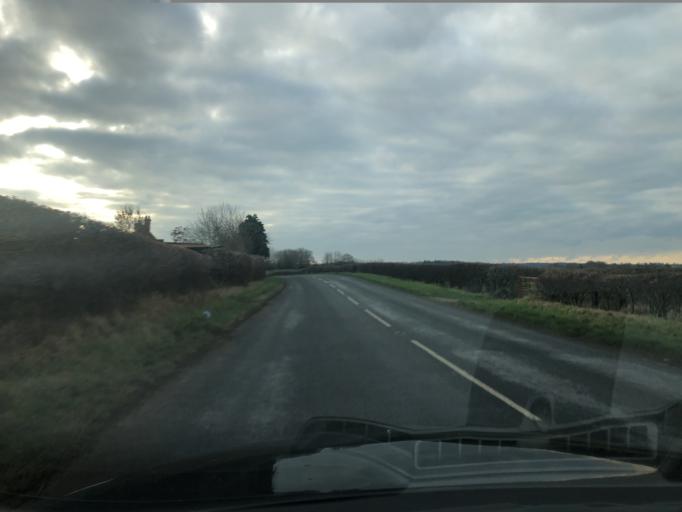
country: GB
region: England
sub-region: North Yorkshire
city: Bedale
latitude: 54.2810
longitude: -1.6013
